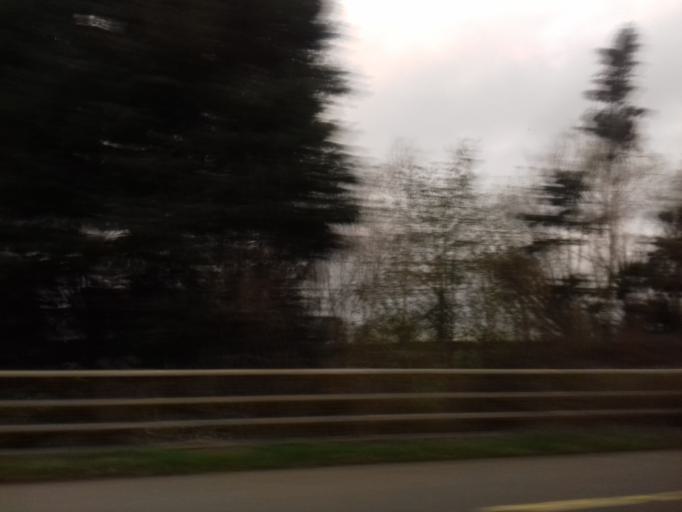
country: IE
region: Munster
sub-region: County Limerick
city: Rathkeale
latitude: 52.5197
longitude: -8.9507
